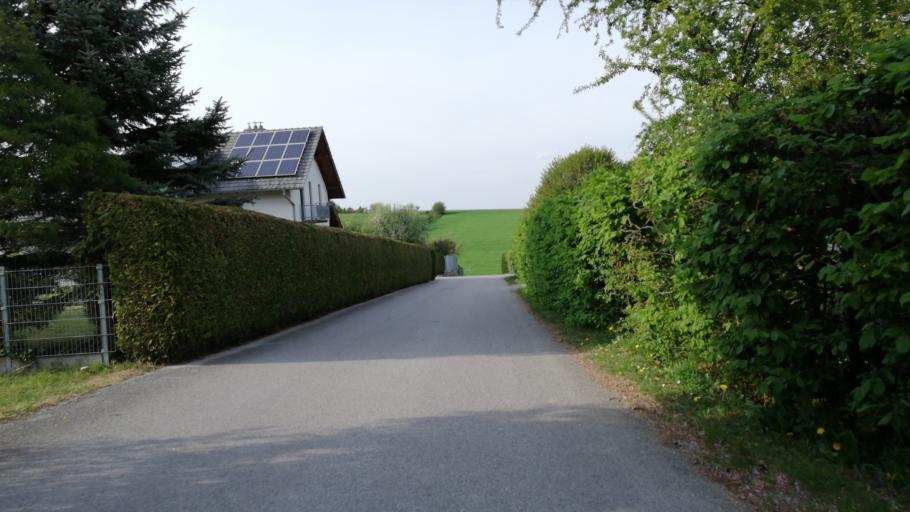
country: AT
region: Upper Austria
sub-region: Politischer Bezirk Grieskirchen
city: Bad Schallerbach
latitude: 48.1960
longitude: 13.9454
